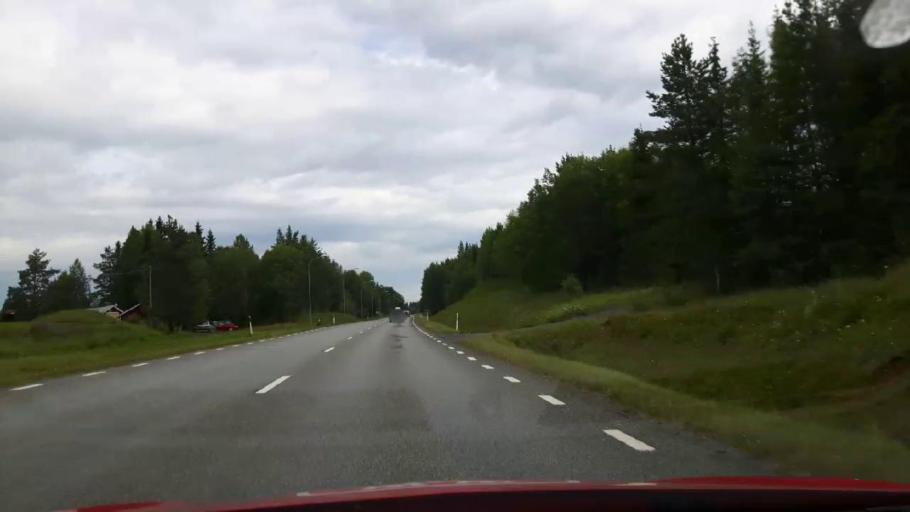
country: SE
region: Jaemtland
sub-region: Stroemsunds Kommun
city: Stroemsund
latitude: 63.6578
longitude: 15.3864
